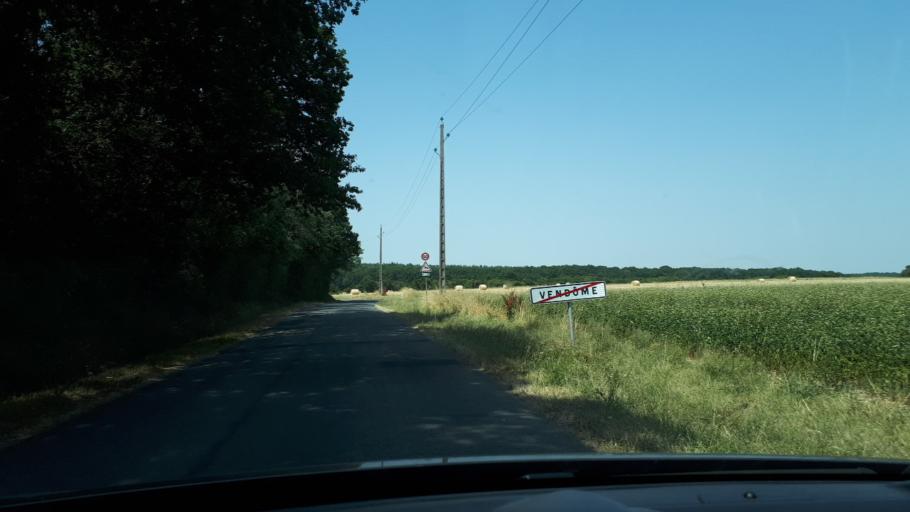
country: FR
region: Centre
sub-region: Departement du Loir-et-Cher
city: Naveil
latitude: 47.8163
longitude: 1.0469
